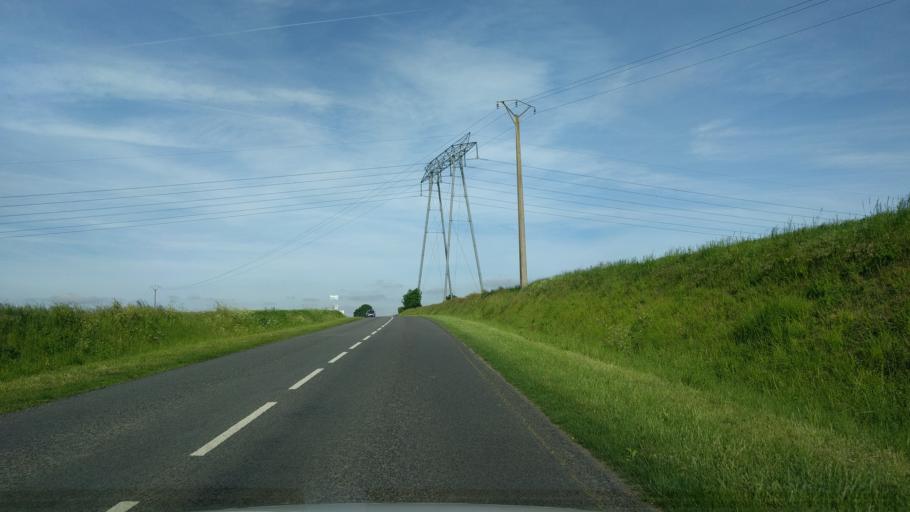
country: FR
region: Picardie
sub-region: Departement de la Somme
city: Peronne
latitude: 49.9587
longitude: 2.8713
